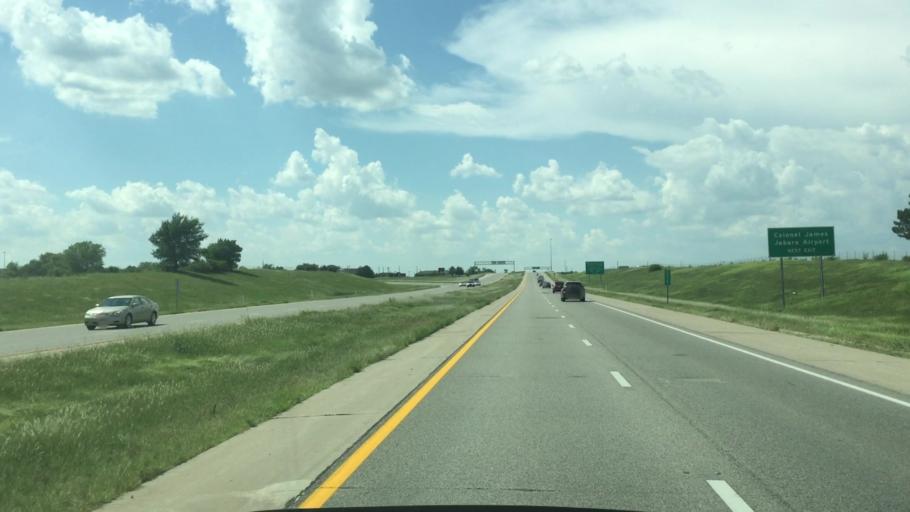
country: US
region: Kansas
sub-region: Sedgwick County
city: Bellaire
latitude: 37.7331
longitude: -97.2203
